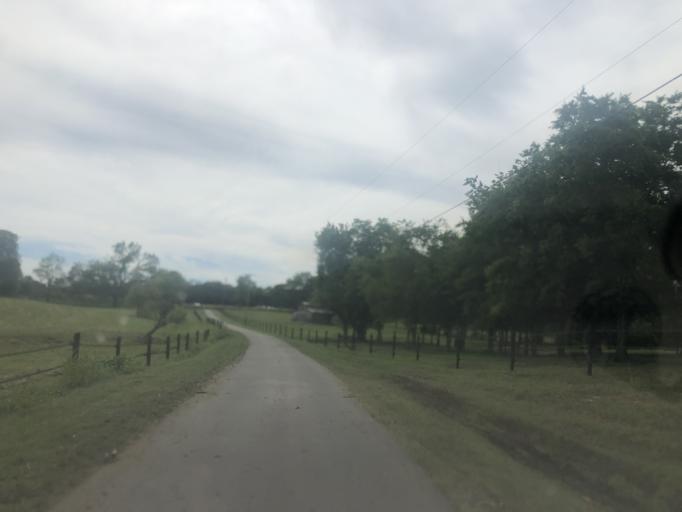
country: US
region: Tennessee
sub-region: Davidson County
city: Lakewood
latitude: 36.2252
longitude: -86.6539
